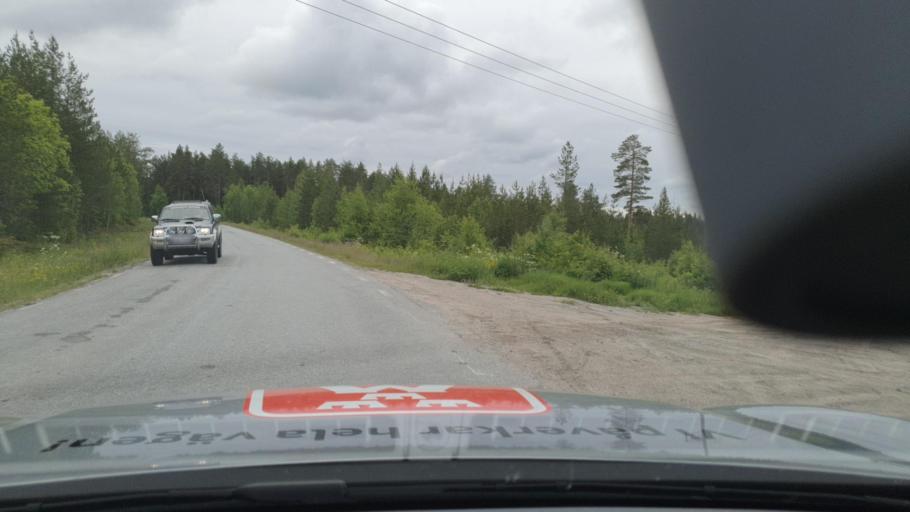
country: SE
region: Norrbotten
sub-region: Lulea Kommun
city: Ranea
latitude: 65.8397
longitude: 22.2970
